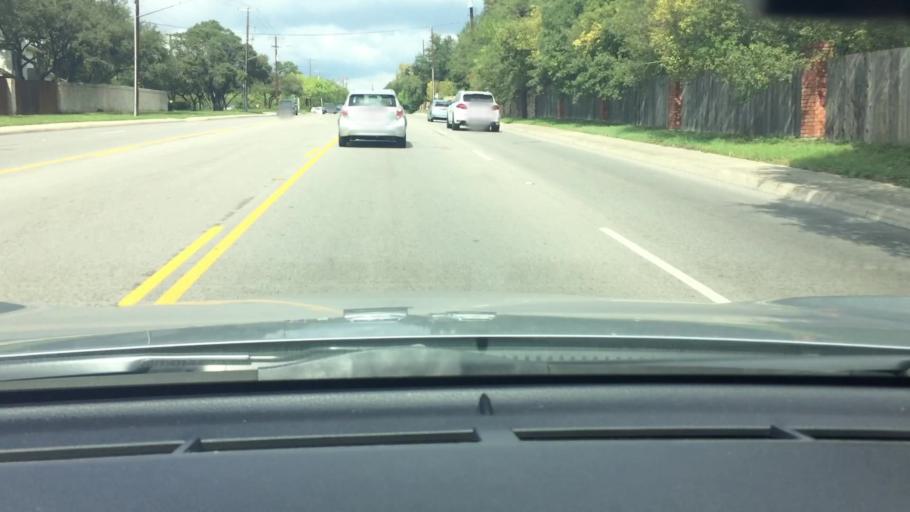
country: US
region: Texas
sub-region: Bexar County
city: Shavano Park
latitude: 29.5608
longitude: -98.5617
